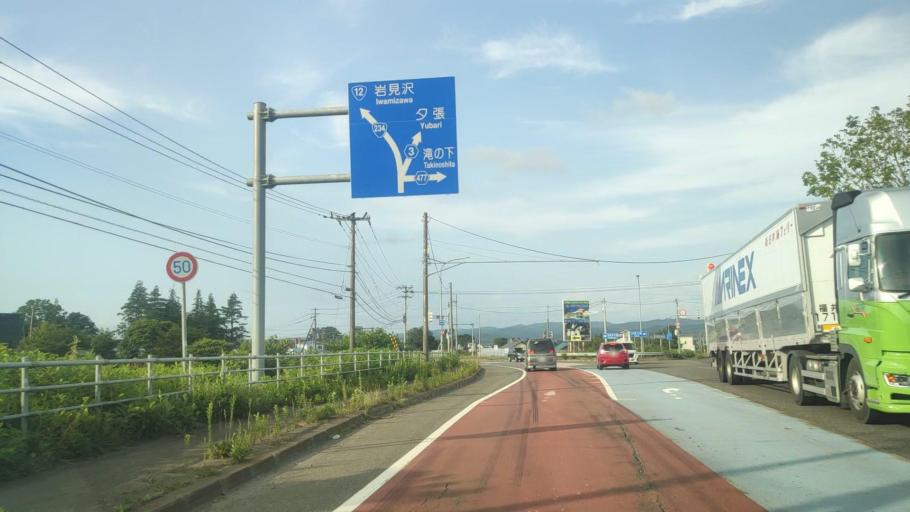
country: JP
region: Hokkaido
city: Iwamizawa
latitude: 43.0253
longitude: 141.8092
